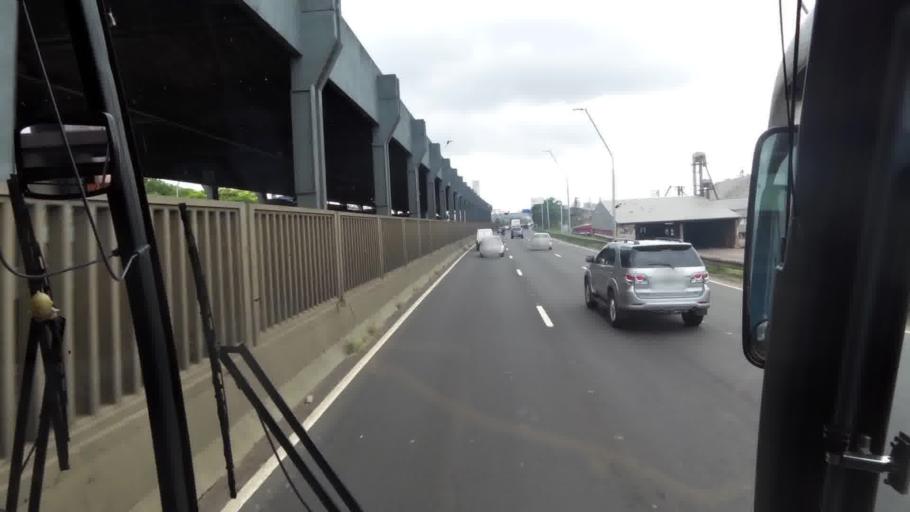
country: BR
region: Rio Grande do Sul
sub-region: Porto Alegre
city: Porto Alegre
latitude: -30.0057
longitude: -51.2093
